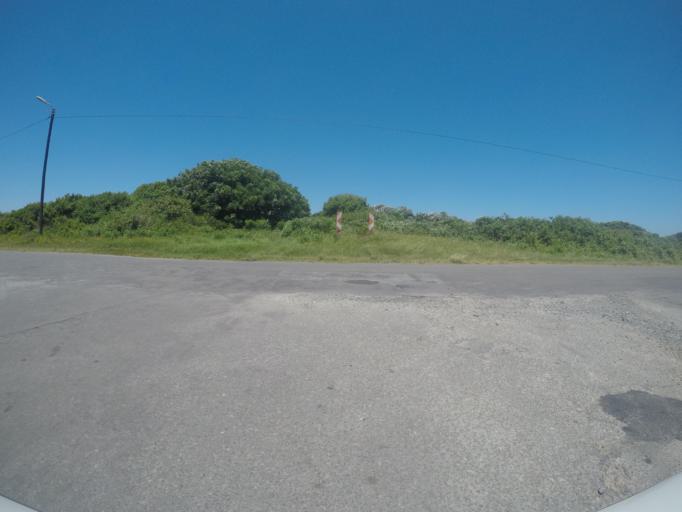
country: ZA
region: Eastern Cape
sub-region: Buffalo City Metropolitan Municipality
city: East London
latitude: -32.9509
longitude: 28.0150
